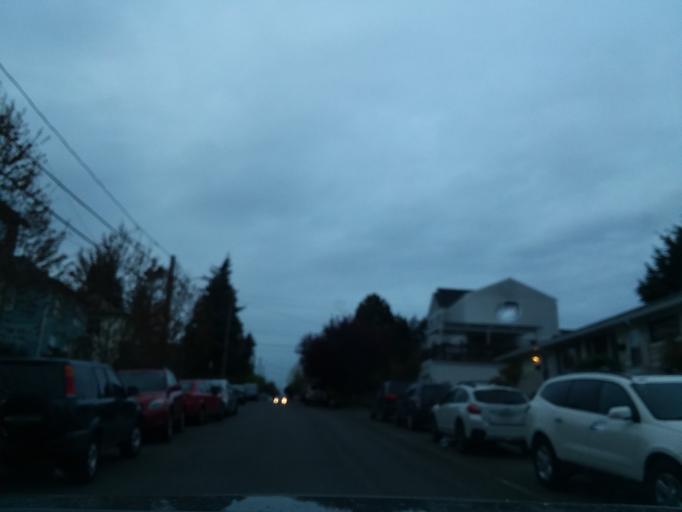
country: US
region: Washington
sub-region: King County
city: Seattle
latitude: 47.6695
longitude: -122.3957
